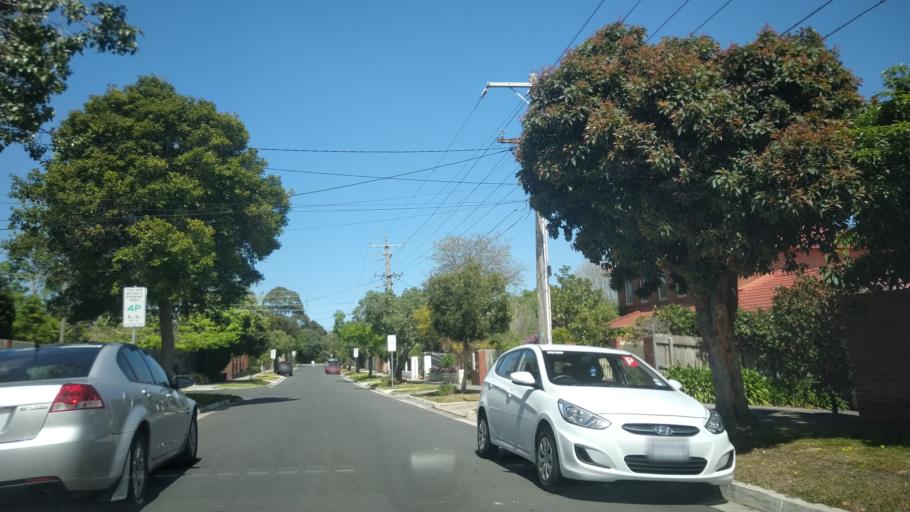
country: AU
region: Victoria
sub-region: Bayside
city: Cheltenham
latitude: -37.9628
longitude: 145.0486
